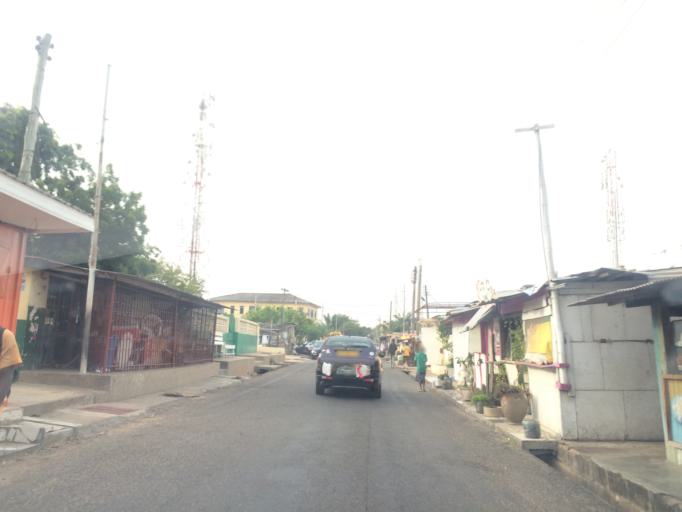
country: GH
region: Greater Accra
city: Accra
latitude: 5.5531
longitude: -0.1868
